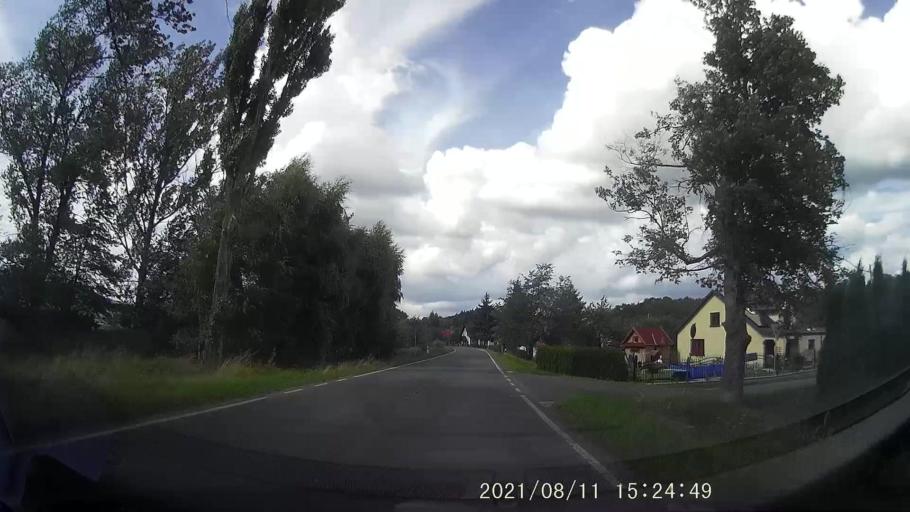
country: PL
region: Lower Silesian Voivodeship
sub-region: Powiat klodzki
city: Bystrzyca Klodzka
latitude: 50.2829
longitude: 16.6813
